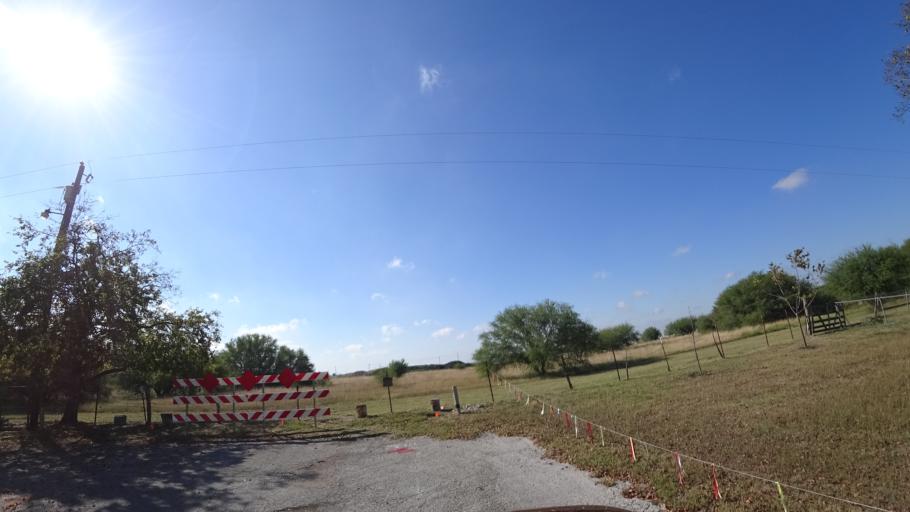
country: US
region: Texas
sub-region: Travis County
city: Windemere
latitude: 30.4380
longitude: -97.6528
